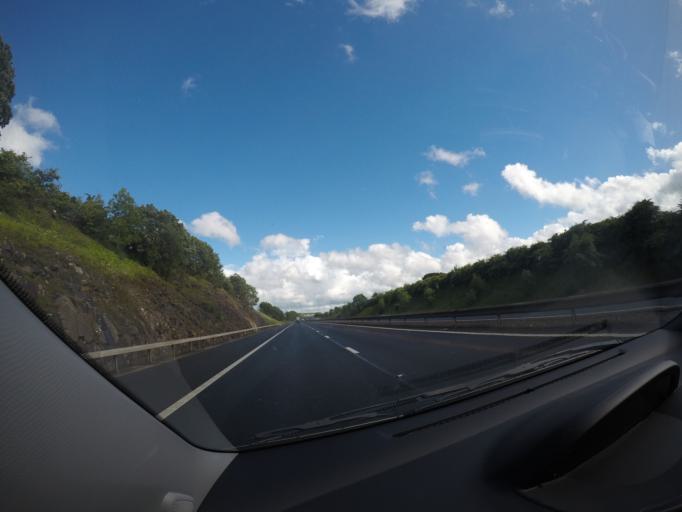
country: GB
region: Scotland
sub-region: South Lanarkshire
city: Lesmahagow
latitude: 55.6340
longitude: -3.8688
